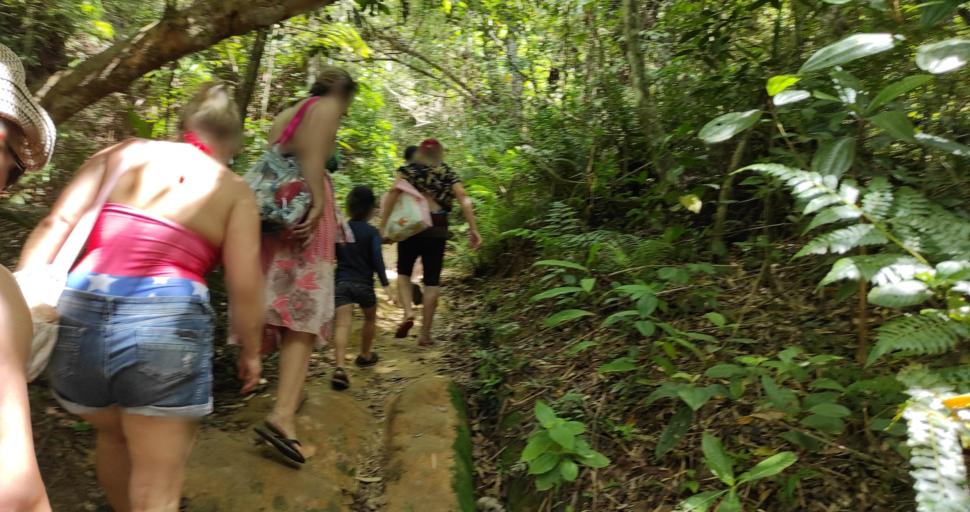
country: BR
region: Santa Catarina
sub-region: Porto Belo
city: Porto Belo
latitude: -27.1958
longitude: -48.5602
